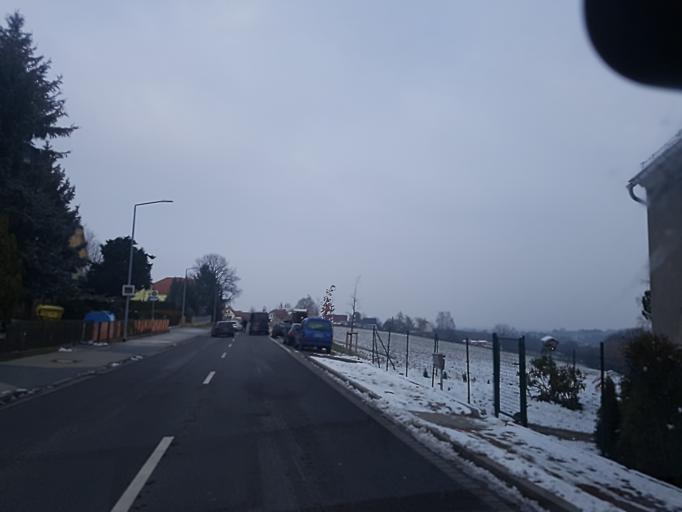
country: DE
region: Saxony
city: Mugeln
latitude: 51.2209
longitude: 13.0028
